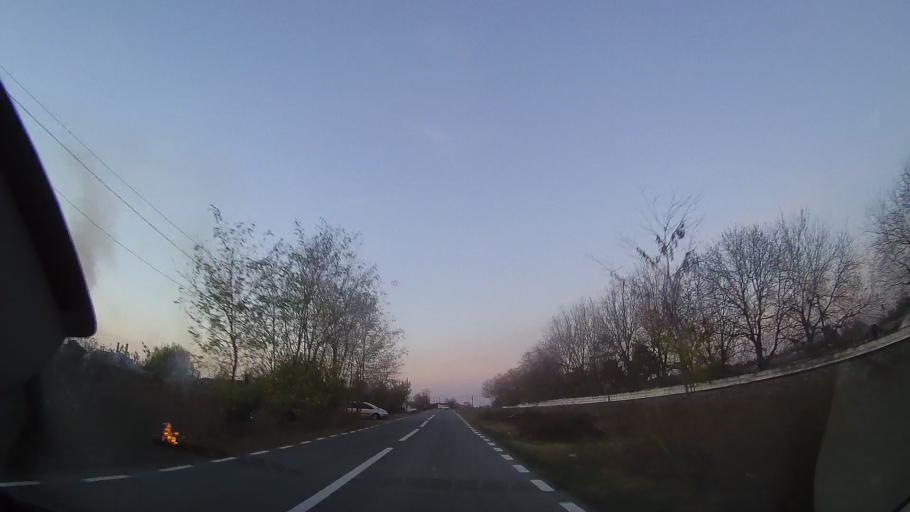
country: RO
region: Constanta
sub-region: Comuna Cobadin
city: Cobadin
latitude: 44.0529
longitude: 28.2471
